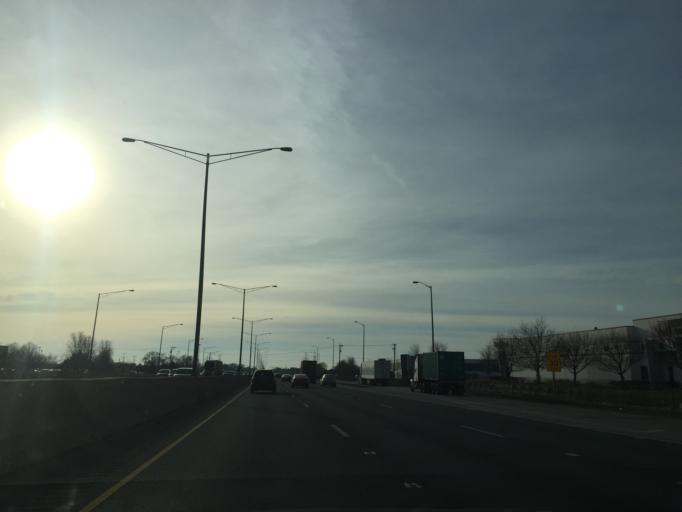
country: US
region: Illinois
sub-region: Will County
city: Bolingbrook
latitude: 41.6764
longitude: -88.0845
